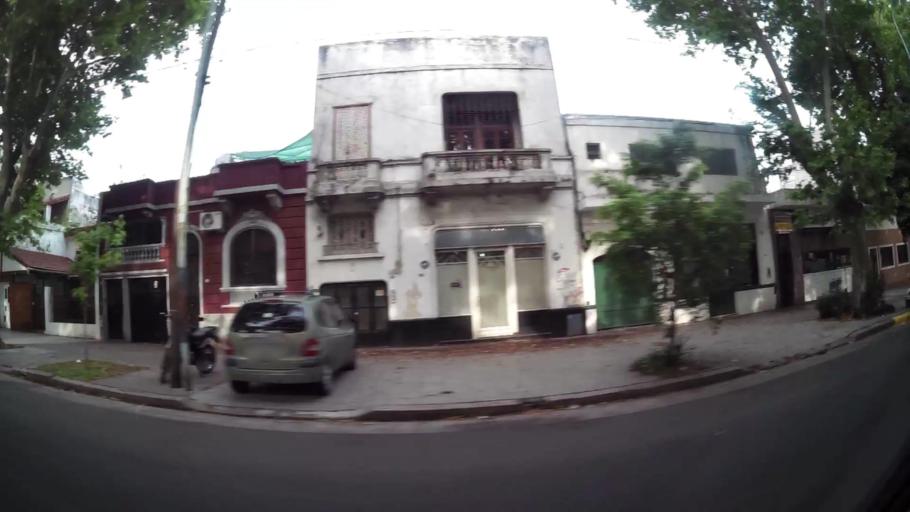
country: AR
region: Buenos Aires F.D.
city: Villa Santa Rita
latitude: -34.6379
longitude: -58.4452
